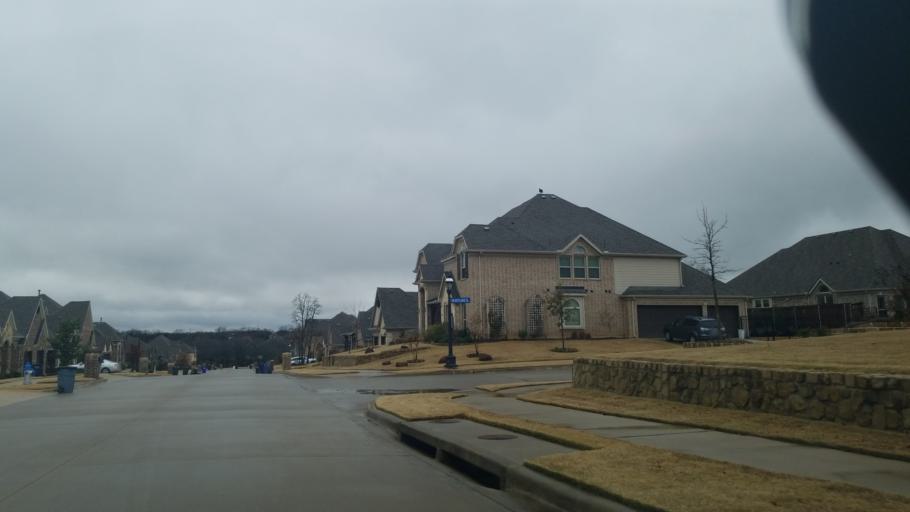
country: US
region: Texas
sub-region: Denton County
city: Corinth
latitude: 33.1451
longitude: -97.0901
